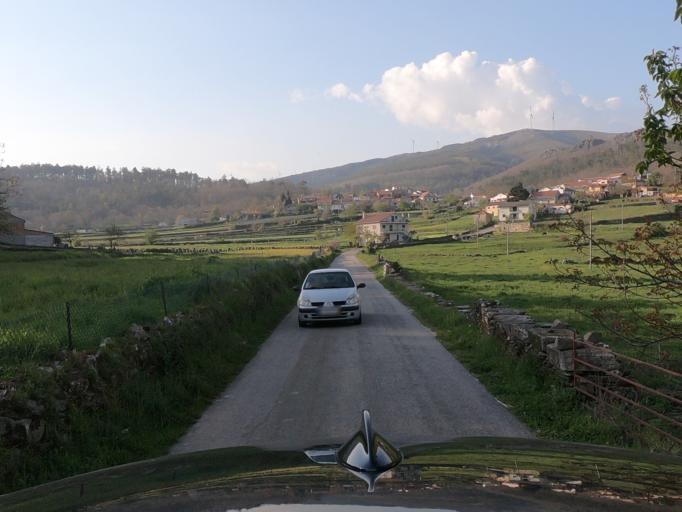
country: PT
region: Vila Real
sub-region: Santa Marta de Penaguiao
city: Santa Marta de Penaguiao
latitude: 41.2942
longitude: -7.8369
